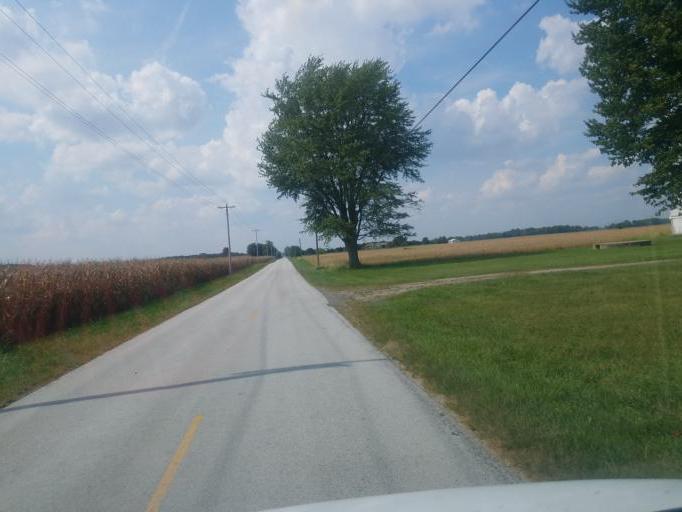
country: US
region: Ohio
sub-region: Hardin County
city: Kenton
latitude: 40.6421
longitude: -83.7377
